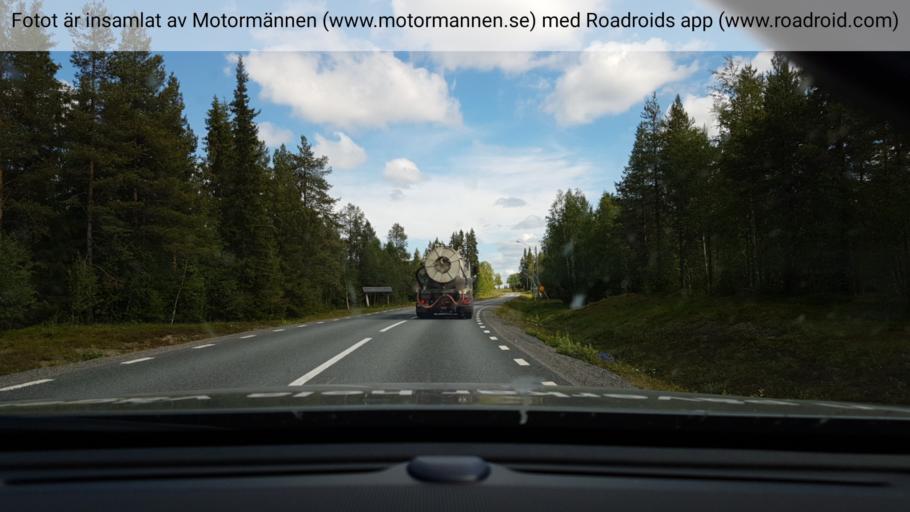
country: SE
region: Vaesterbotten
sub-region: Sorsele Kommun
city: Sorsele
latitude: 65.5580
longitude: 17.8404
